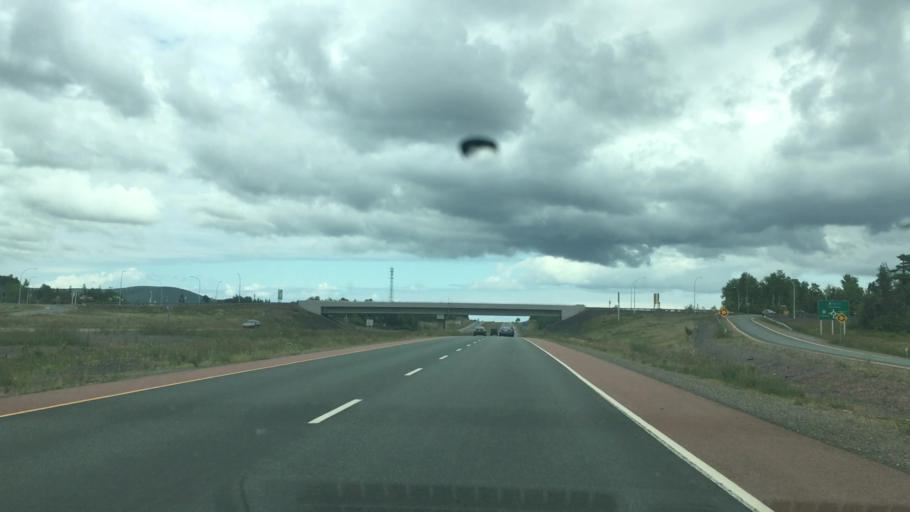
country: CA
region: Nova Scotia
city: Antigonish
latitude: 45.5995
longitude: -62.0265
